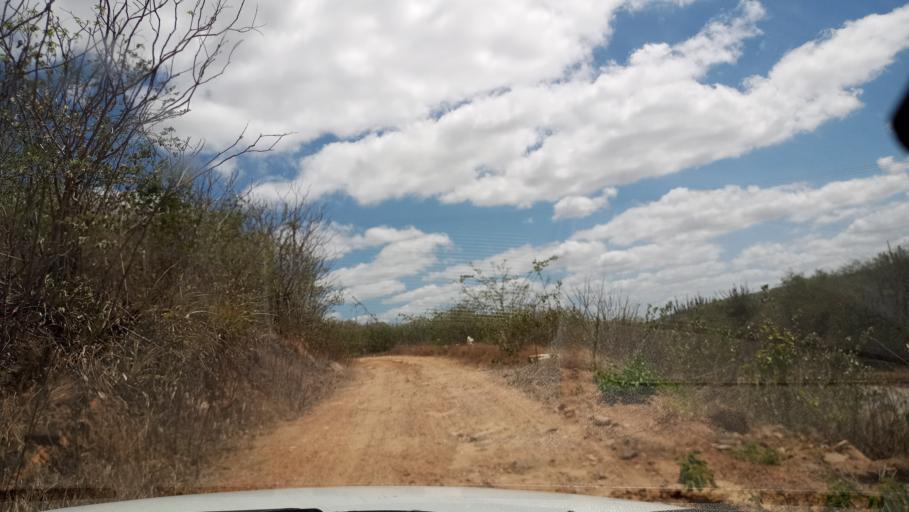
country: BR
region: Rio Grande do Norte
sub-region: Sao Paulo Do Potengi
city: Sao Paulo do Potengi
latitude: -5.7483
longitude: -35.9111
